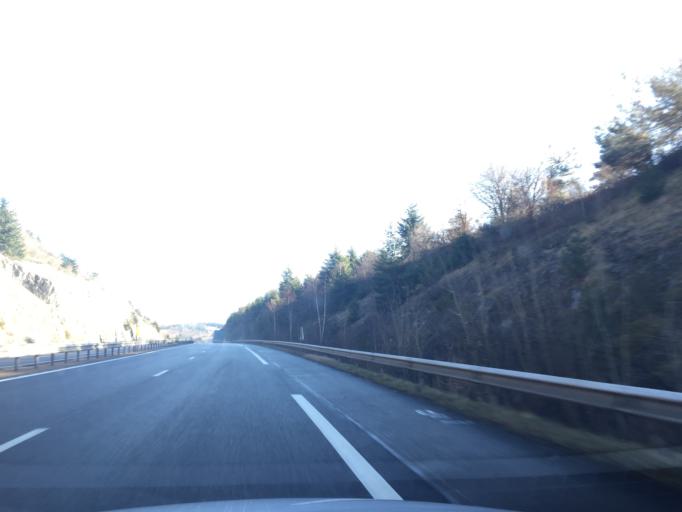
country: FR
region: Rhone-Alpes
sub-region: Departement de la Loire
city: Saint-Just-en-Chevalet
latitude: 45.8769
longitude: 3.8824
